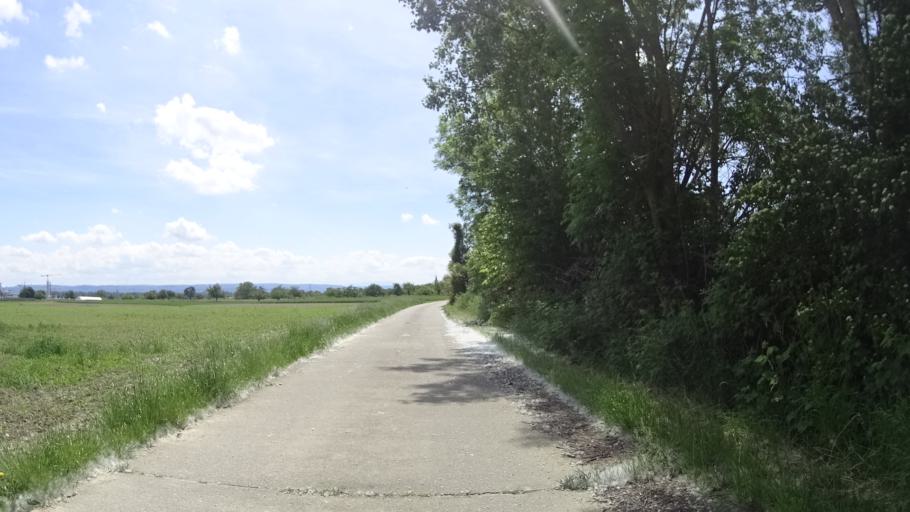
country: DE
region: Baden-Wuerttemberg
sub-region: Freiburg Region
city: Schwanau
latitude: 48.3603
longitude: 7.7562
